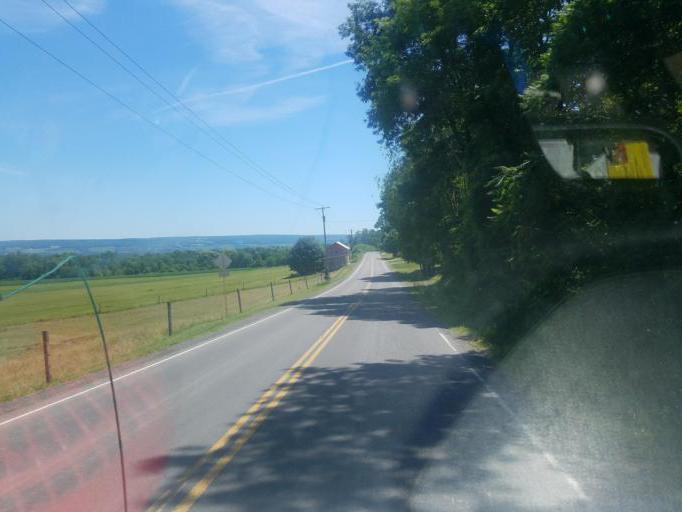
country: US
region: New York
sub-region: Yates County
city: Dundee
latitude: 42.5974
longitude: -76.9638
